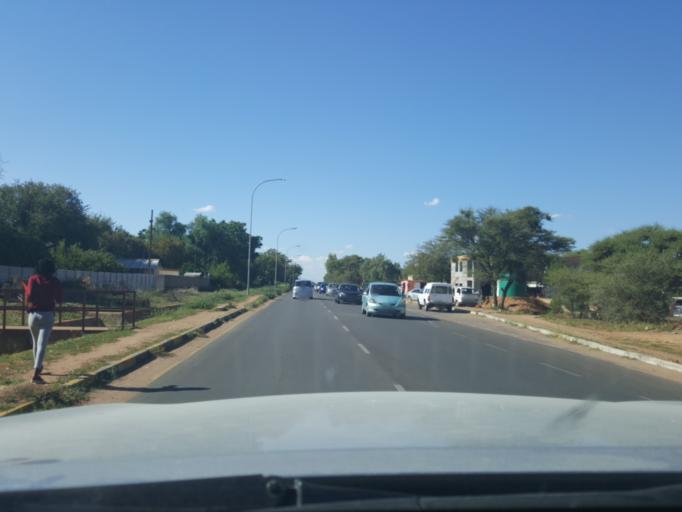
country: BW
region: South East
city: Gaborone
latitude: -24.6204
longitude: 25.9442
